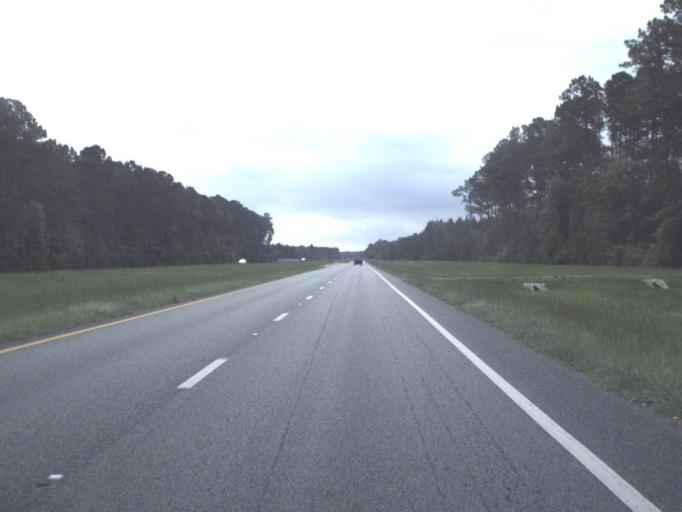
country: US
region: Florida
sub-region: Nassau County
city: Yulee
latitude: 30.6153
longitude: -81.7049
